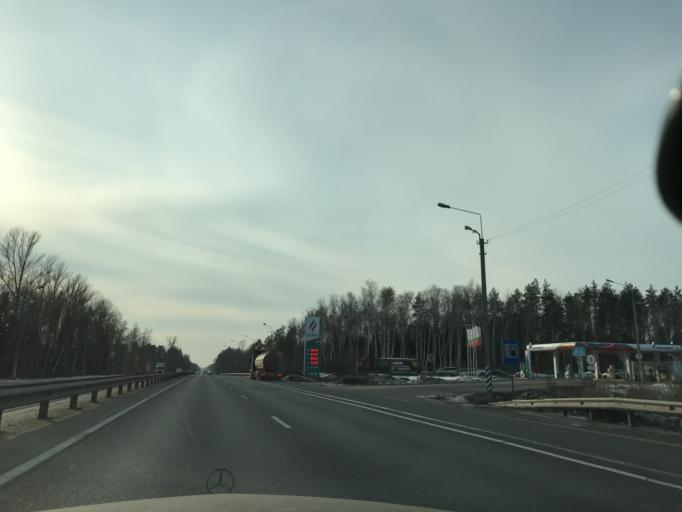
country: RU
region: Vladimir
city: Novki
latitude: 56.2013
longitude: 41.0974
